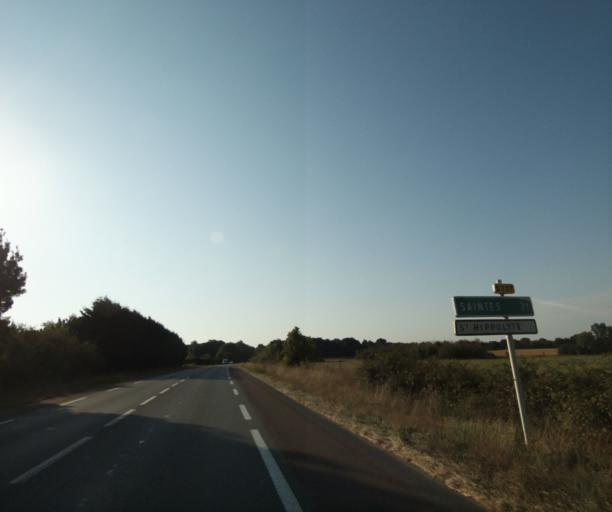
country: FR
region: Poitou-Charentes
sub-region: Departement de la Charente-Maritime
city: Tonnay-Charente
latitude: 45.9498
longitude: -0.8686
